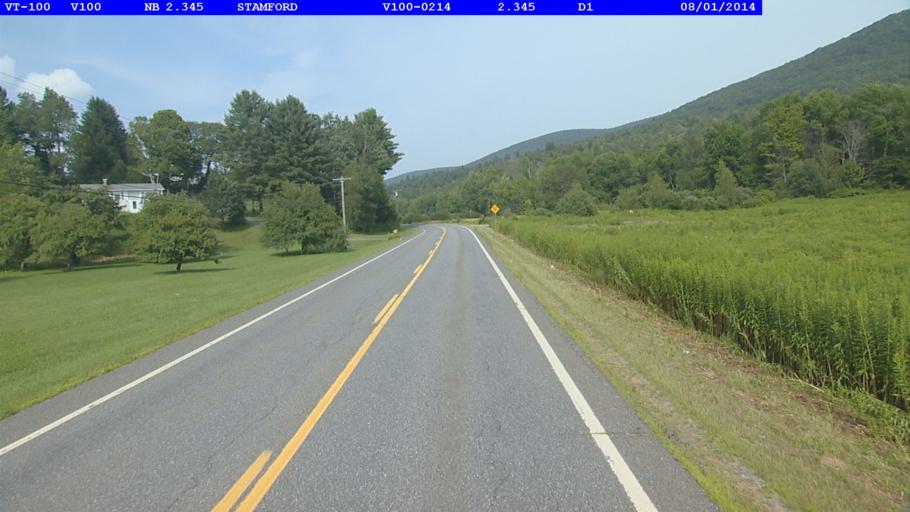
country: US
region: Massachusetts
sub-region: Berkshire County
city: North Adams
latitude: 42.7692
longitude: -73.0535
